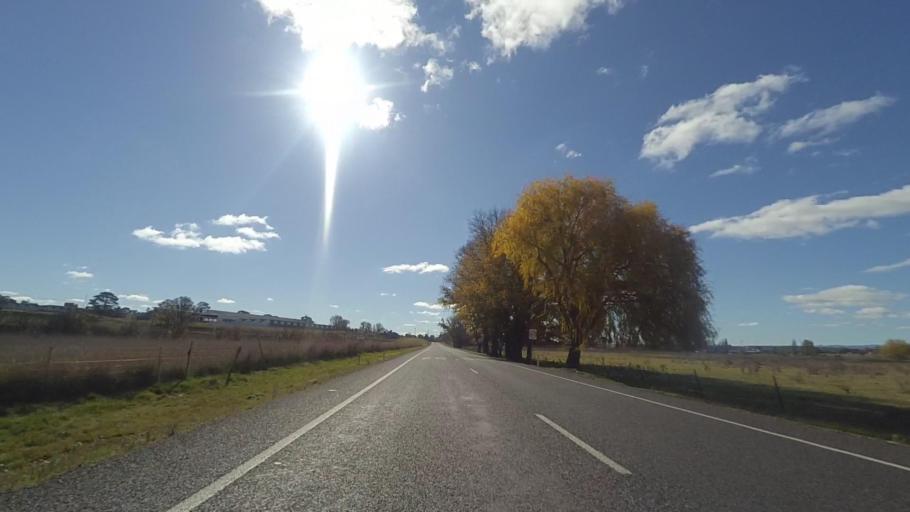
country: AU
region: New South Wales
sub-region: Bathurst Regional
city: Bathurst
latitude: -33.4464
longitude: 149.5789
